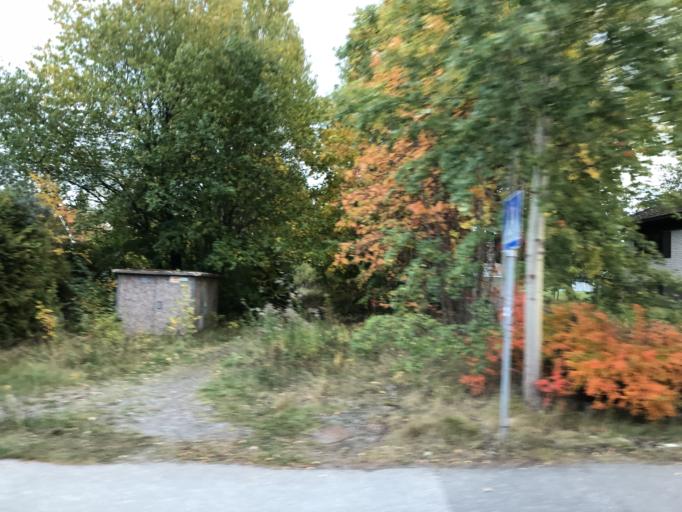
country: SE
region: Stockholm
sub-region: Jarfalla Kommun
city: Jakobsberg
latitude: 59.4275
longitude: 17.8125
